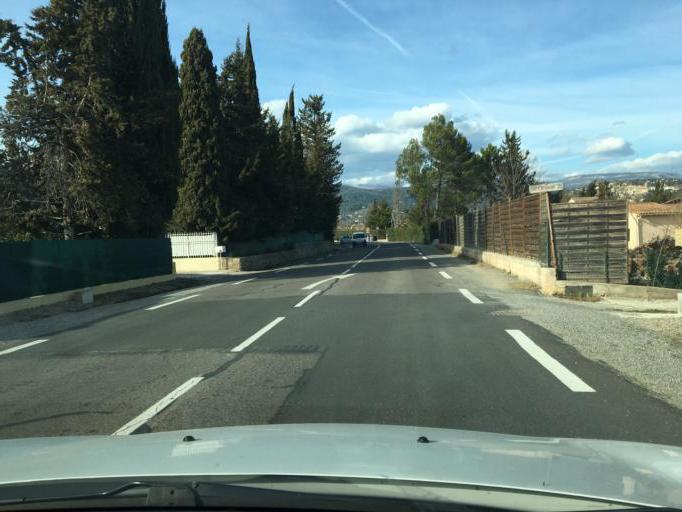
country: FR
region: Provence-Alpes-Cote d'Azur
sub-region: Departement du Var
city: Fayence
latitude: 43.6031
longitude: 6.6882
